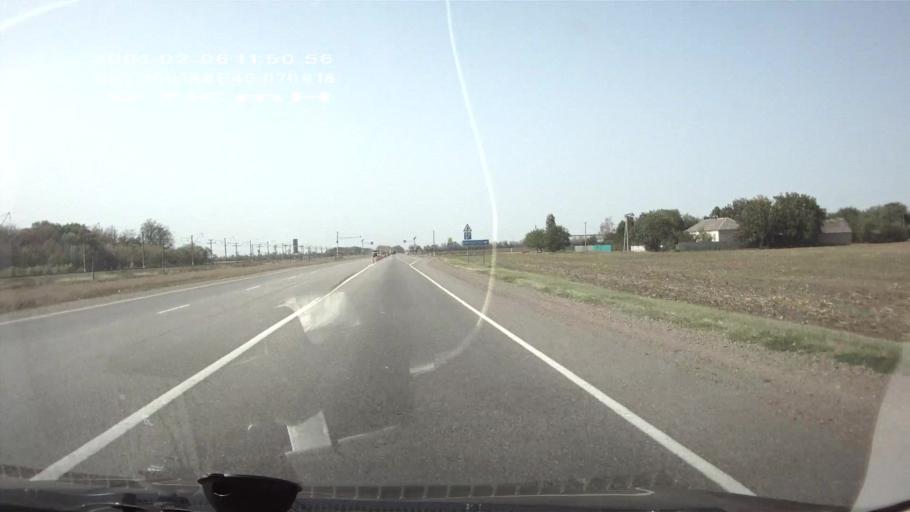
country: RU
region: Krasnodarskiy
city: Tbilisskaya
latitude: 45.3601
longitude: 40.0695
